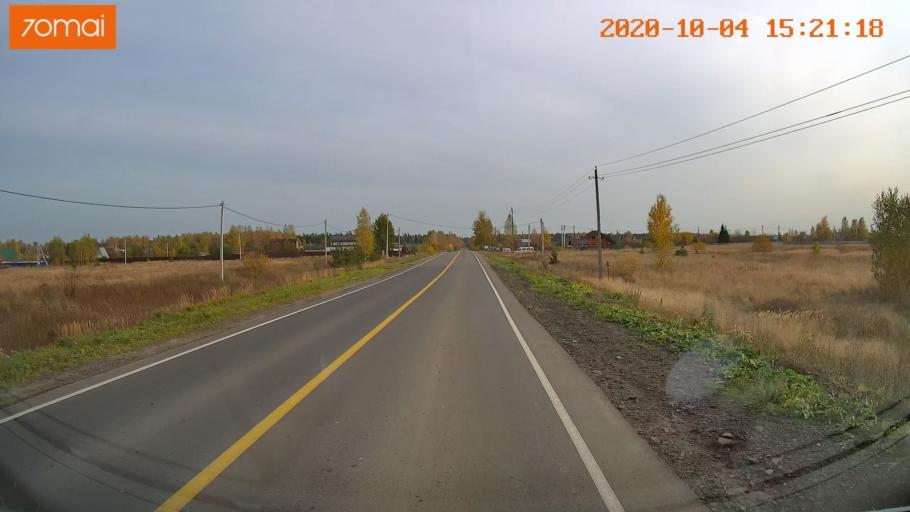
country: RU
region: Ivanovo
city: Bogorodskoye
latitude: 57.0872
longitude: 40.9211
